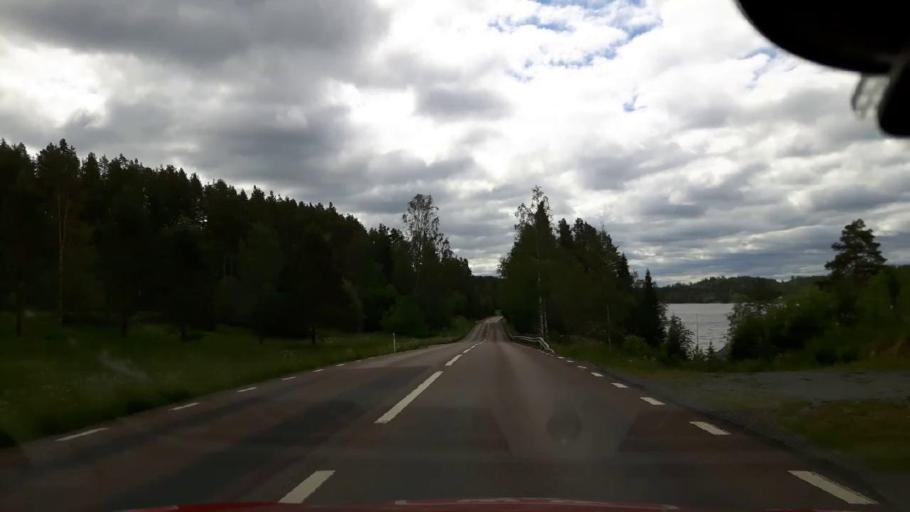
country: SE
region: Jaemtland
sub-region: OEstersunds Kommun
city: Brunflo
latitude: 63.0124
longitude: 14.9520
